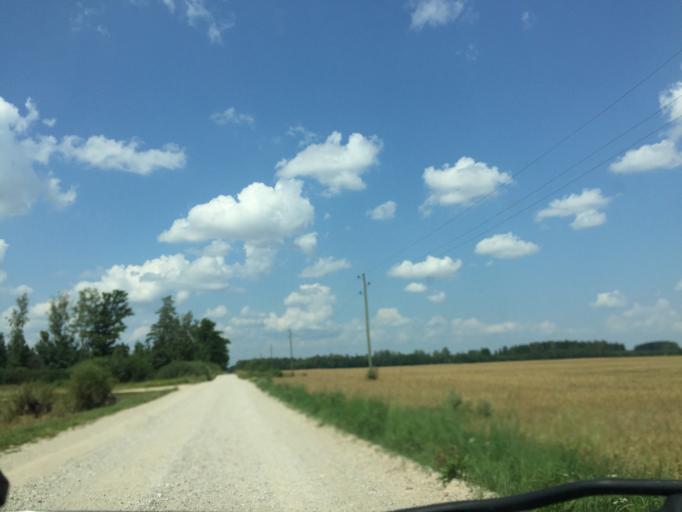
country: LT
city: Zagare
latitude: 56.3802
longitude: 23.2751
